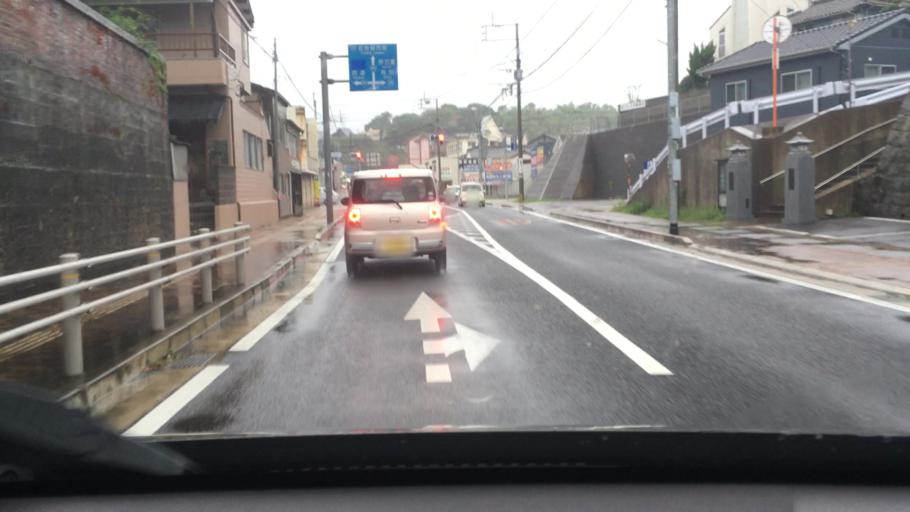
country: JP
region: Nagasaki
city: Sasebo
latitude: 33.1379
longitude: 129.7956
